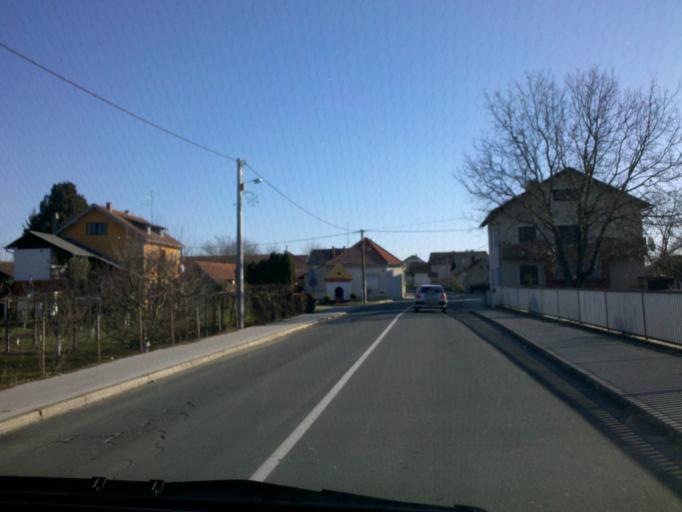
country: HR
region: Medimurska
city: Kotoriba
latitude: 46.3301
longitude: 16.7850
